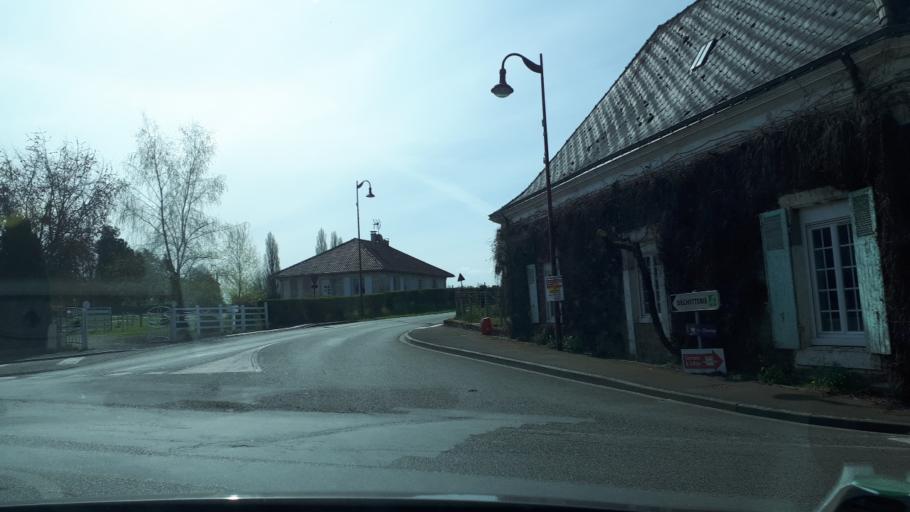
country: FR
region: Pays de la Loire
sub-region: Departement de la Sarthe
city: Cerans-Foulletourte
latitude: 47.8080
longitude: 0.1054
